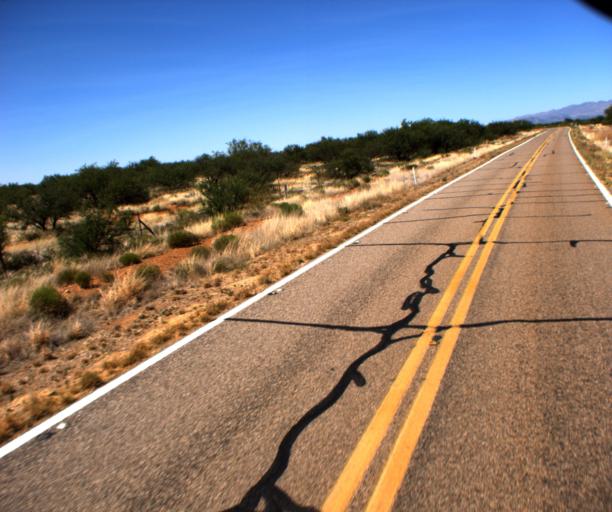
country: US
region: Arizona
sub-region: Pima County
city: Arivaca Junction
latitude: 31.6636
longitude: -111.4906
